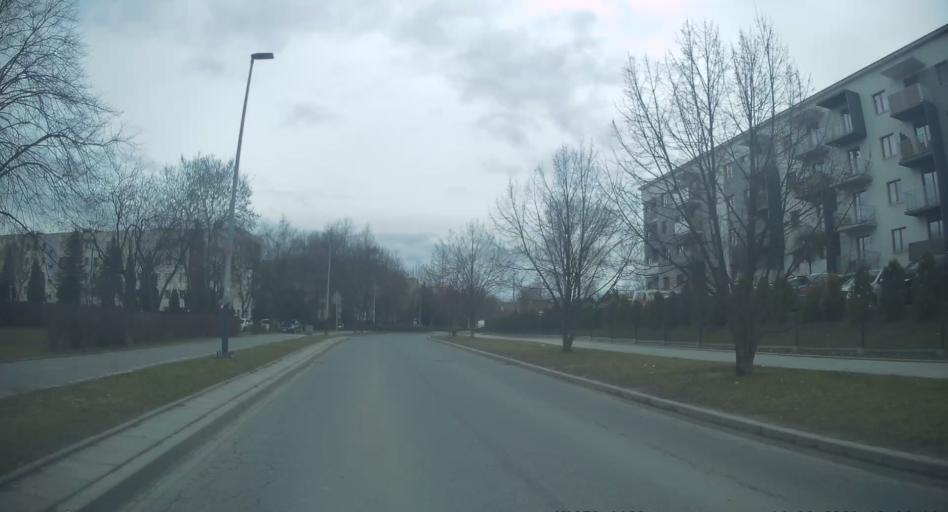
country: PL
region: Lesser Poland Voivodeship
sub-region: Powiat wielicki
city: Czarnochowice
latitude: 50.0155
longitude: 20.0165
